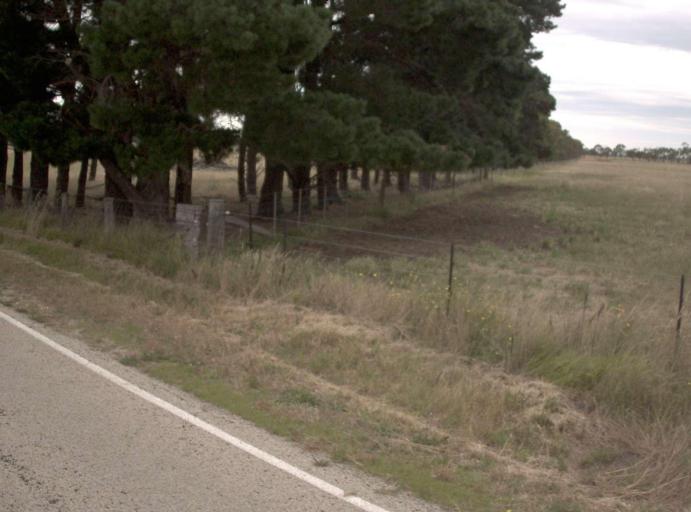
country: AU
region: Victoria
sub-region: East Gippsland
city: Bairnsdale
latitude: -37.9278
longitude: 147.5410
